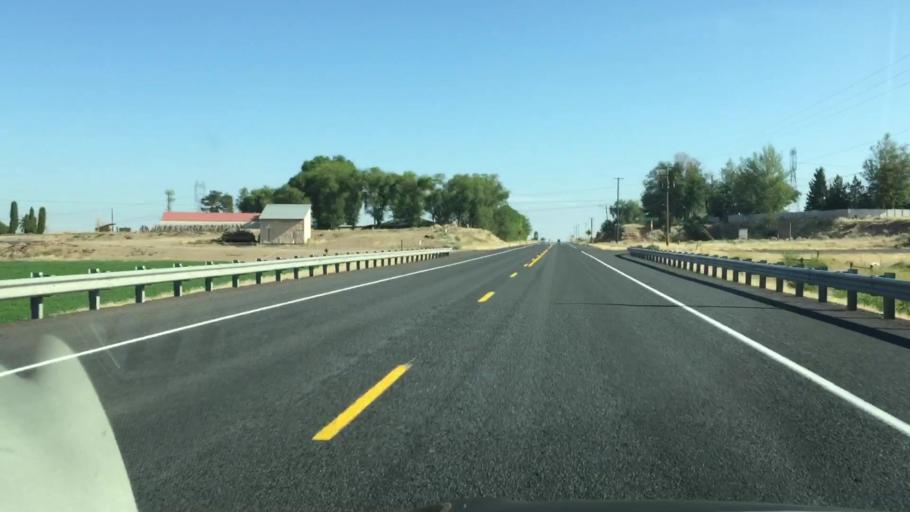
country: US
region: Oregon
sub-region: Jefferson County
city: Culver
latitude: 44.5688
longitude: -121.1611
